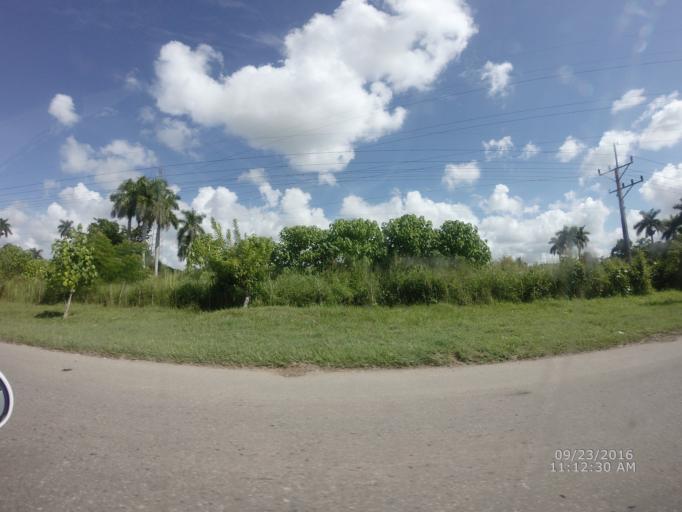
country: CU
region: La Habana
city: Arroyo Naranjo
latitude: 23.0298
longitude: -82.2847
